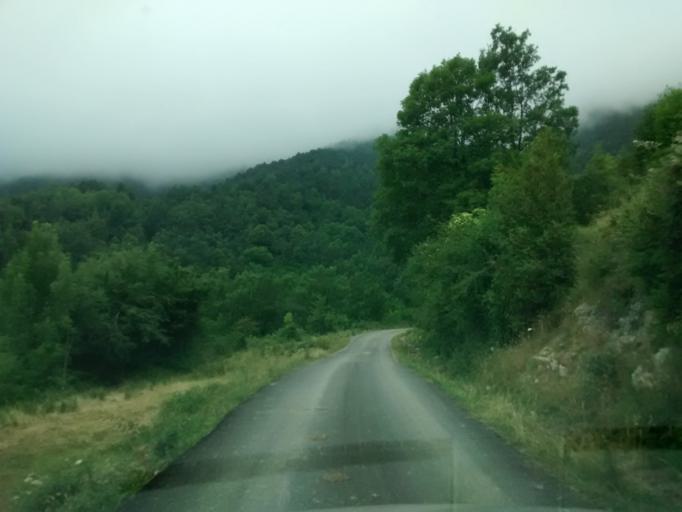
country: ES
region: Aragon
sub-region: Provincia de Huesca
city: Puertolas
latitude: 42.5952
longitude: 0.1276
